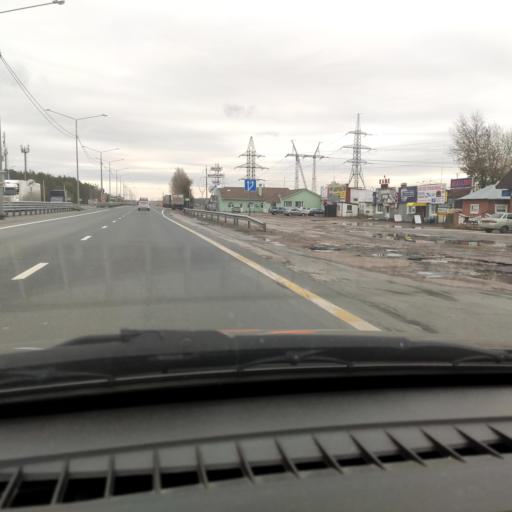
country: RU
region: Samara
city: Zhigulevsk
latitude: 53.5137
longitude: 49.6083
